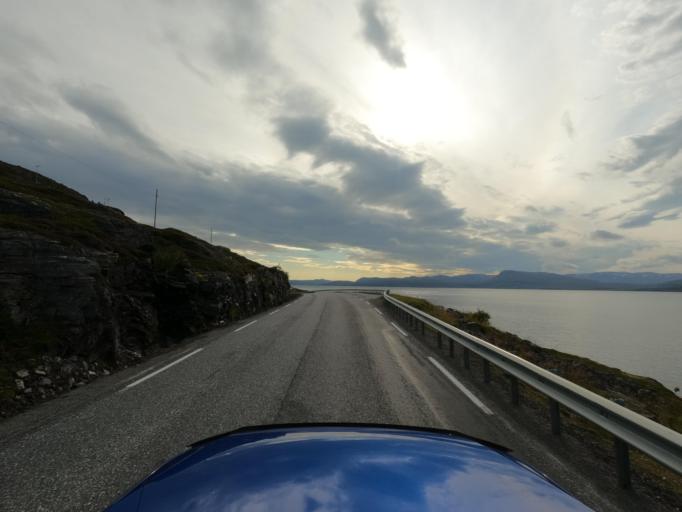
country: NO
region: Finnmark Fylke
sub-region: Hammerfest
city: Rypefjord
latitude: 70.5915
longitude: 23.6810
